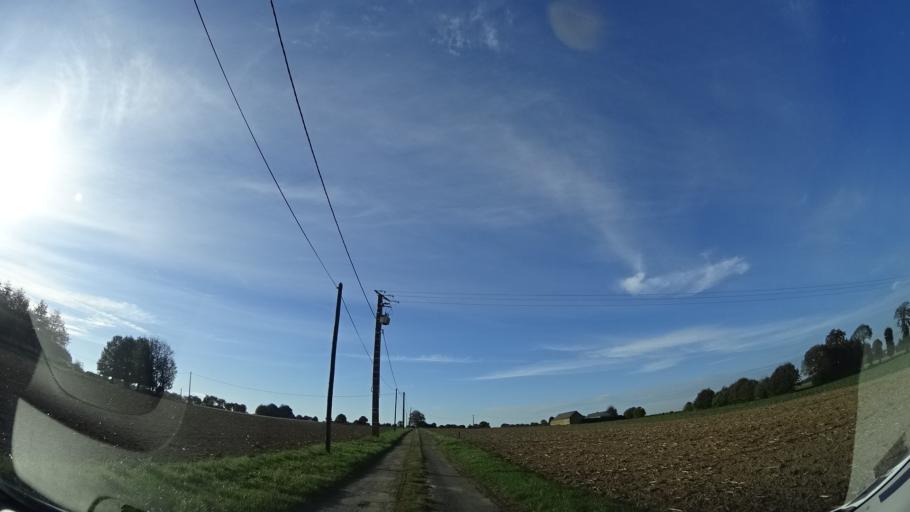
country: FR
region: Brittany
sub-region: Departement d'Ille-et-Vilaine
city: Geveze
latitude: 48.2082
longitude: -1.8239
